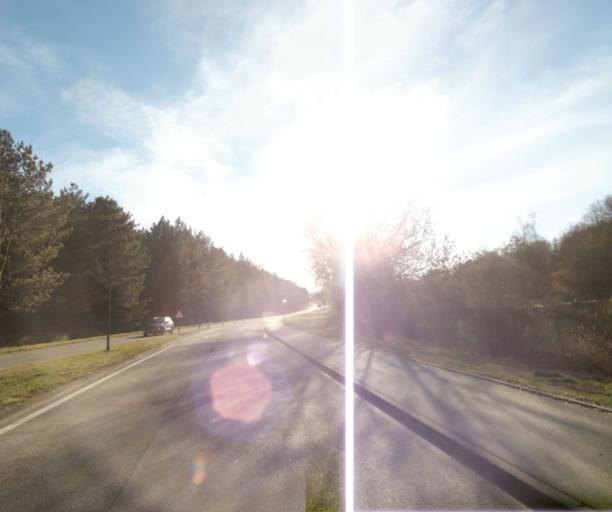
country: FR
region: Lorraine
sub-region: Departement de Meurthe-et-Moselle
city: Chavigny
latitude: 48.6585
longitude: 6.1182
